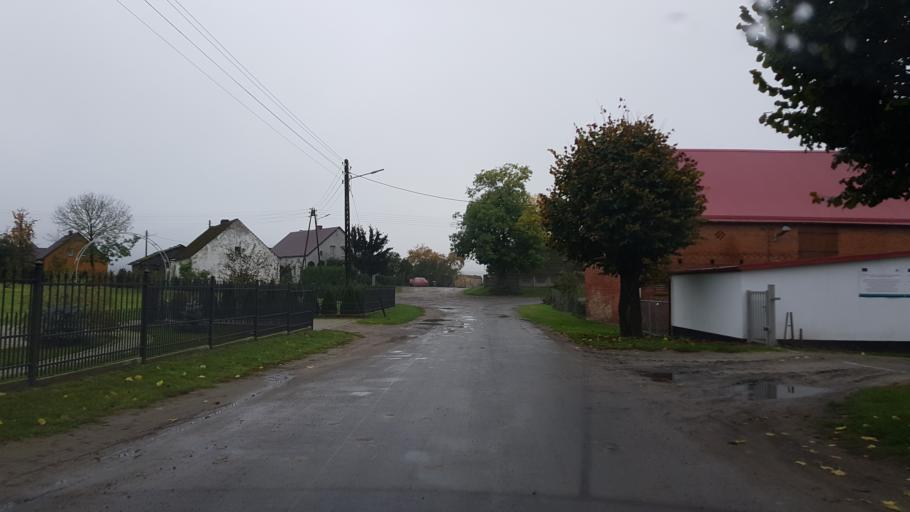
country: PL
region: West Pomeranian Voivodeship
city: Trzcinsko Zdroj
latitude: 53.0582
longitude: 14.5350
